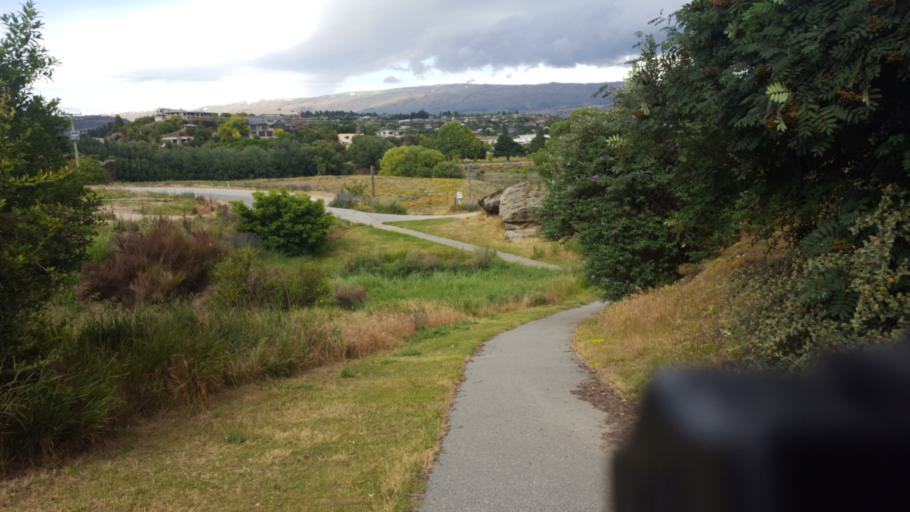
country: NZ
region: Otago
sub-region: Queenstown-Lakes District
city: Wanaka
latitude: -45.2543
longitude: 169.3999
